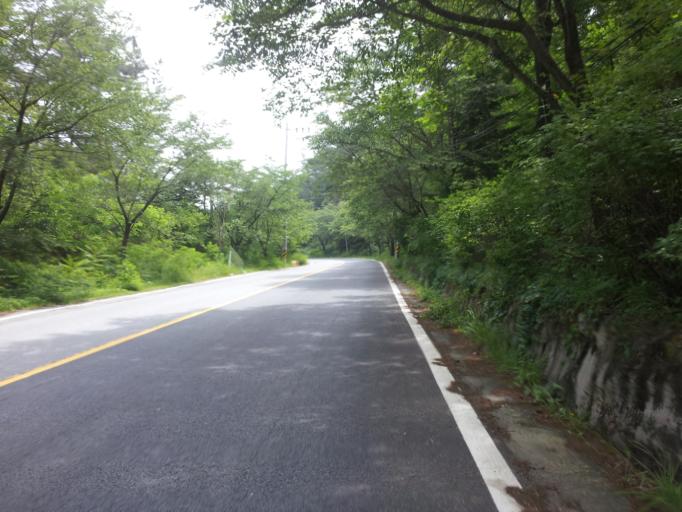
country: KR
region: Chungcheongbuk-do
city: Okcheon
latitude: 36.3909
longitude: 127.5239
